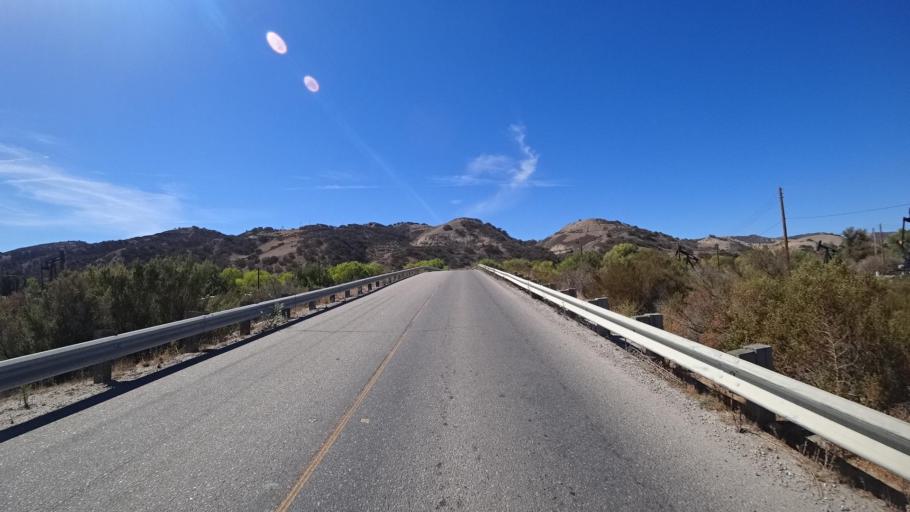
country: US
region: California
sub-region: San Luis Obispo County
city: Lake Nacimiento
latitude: 35.9622
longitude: -120.8799
